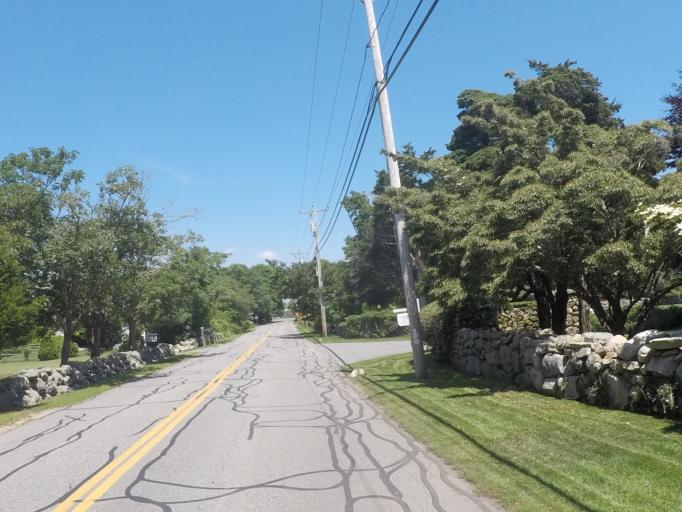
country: US
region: Massachusetts
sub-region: Bristol County
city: Bliss Corner
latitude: 41.5392
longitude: -70.9522
